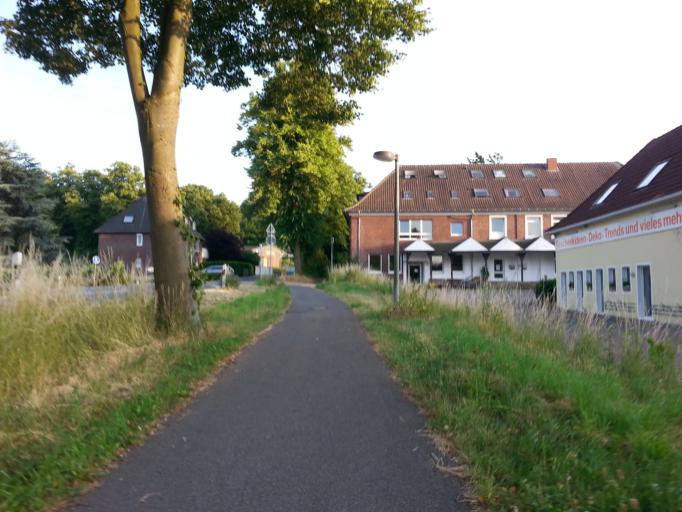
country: DE
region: North Rhine-Westphalia
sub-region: Regierungsbezirk Munster
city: Havixbeck
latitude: 51.9679
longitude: 7.4074
